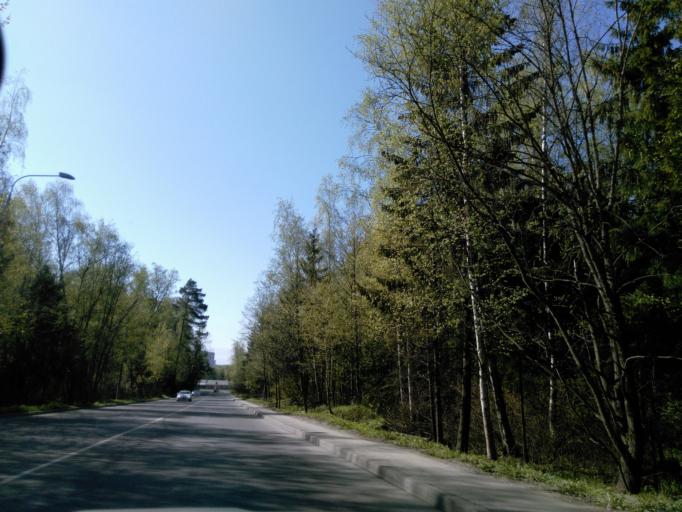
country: RU
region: Moskovskaya
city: Chashnikovo
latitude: 56.0106
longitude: 37.1804
